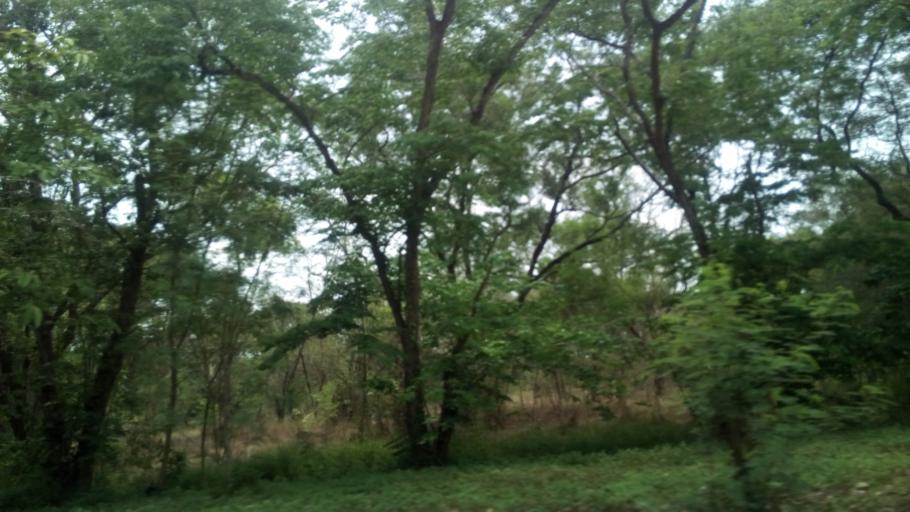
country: TH
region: Bangkok
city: Thawi Watthana
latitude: 13.7790
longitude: 100.3108
